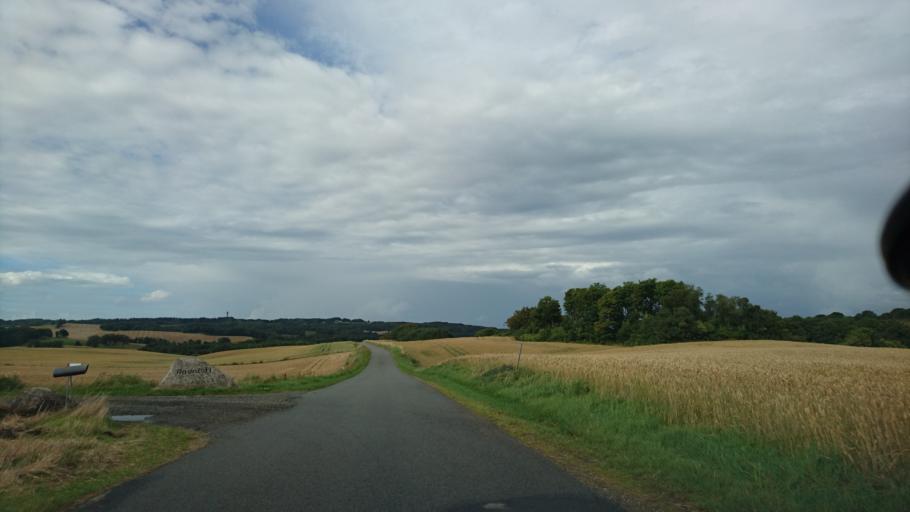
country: DK
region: North Denmark
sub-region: Frederikshavn Kommune
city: Saeby
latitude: 57.3915
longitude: 10.4782
